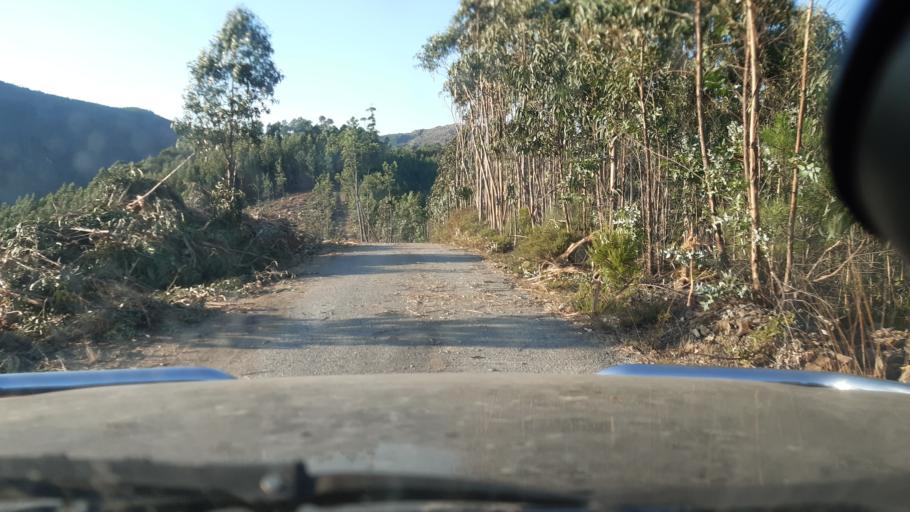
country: PT
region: Viseu
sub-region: Mortagua
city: Mortagua
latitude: 40.5244
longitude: -8.2538
